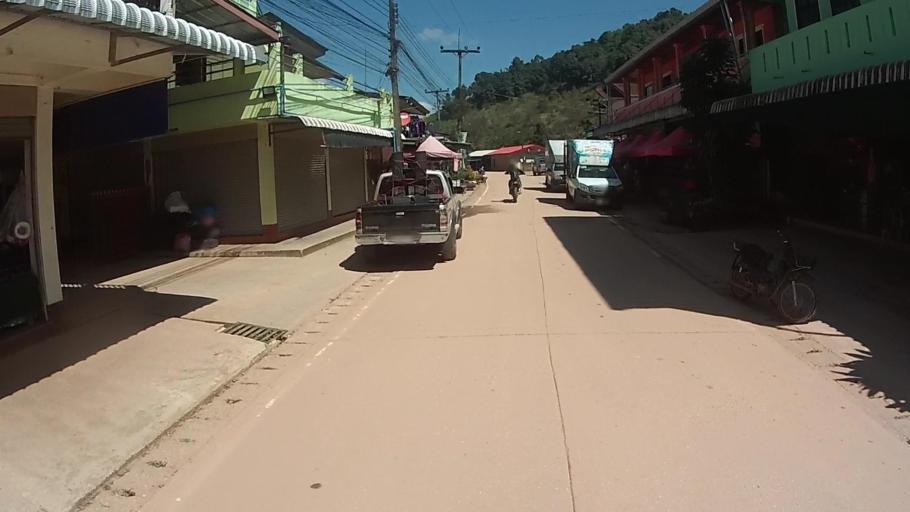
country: TH
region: Chiang Mai
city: Phrao
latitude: 19.4982
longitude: 99.3288
